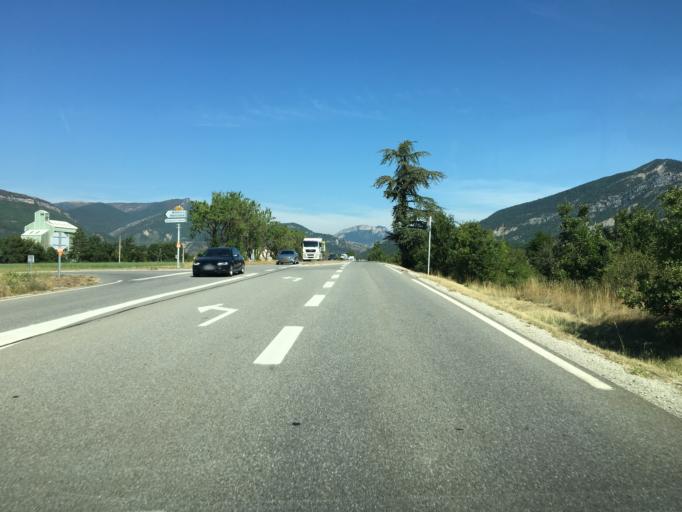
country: FR
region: Provence-Alpes-Cote d'Azur
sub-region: Departement des Hautes-Alpes
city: Serres
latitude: 44.3963
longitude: 5.7369
